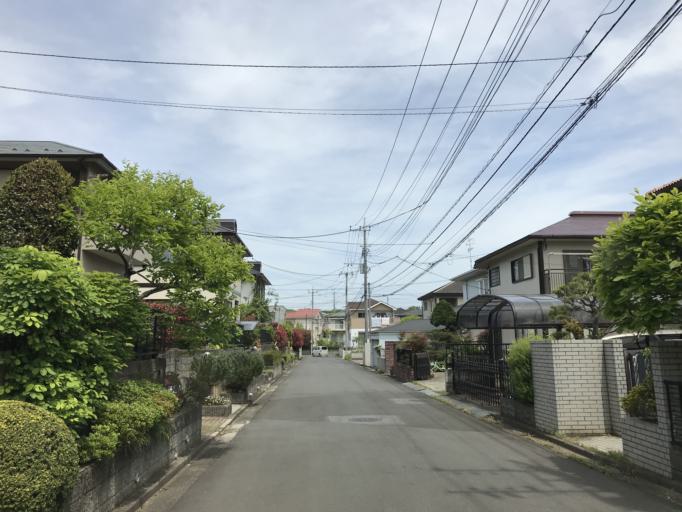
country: JP
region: Ibaraki
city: Mitsukaido
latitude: 35.9710
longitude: 139.9577
